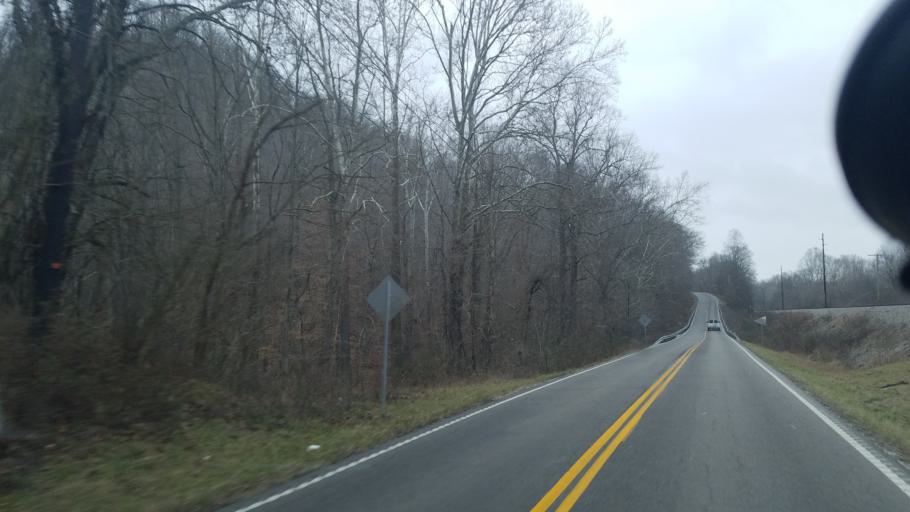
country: US
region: Ohio
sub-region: Scioto County
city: West Portsmouth
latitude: 38.6692
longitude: -83.0898
